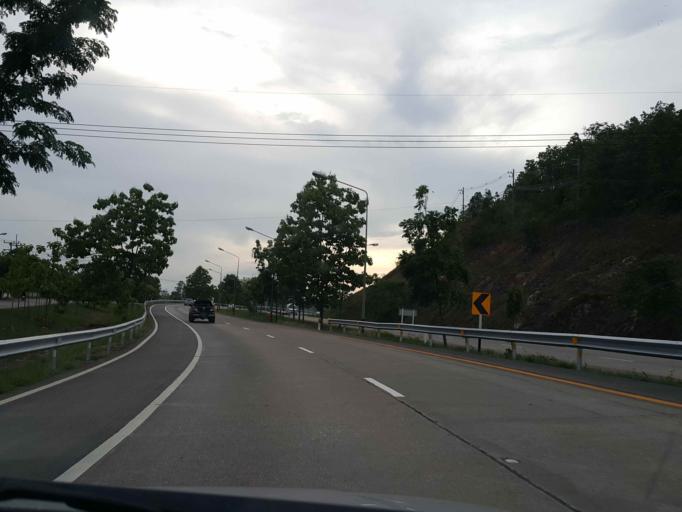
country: TH
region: Lamphun
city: Mae Tha
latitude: 18.4635
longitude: 99.1308
